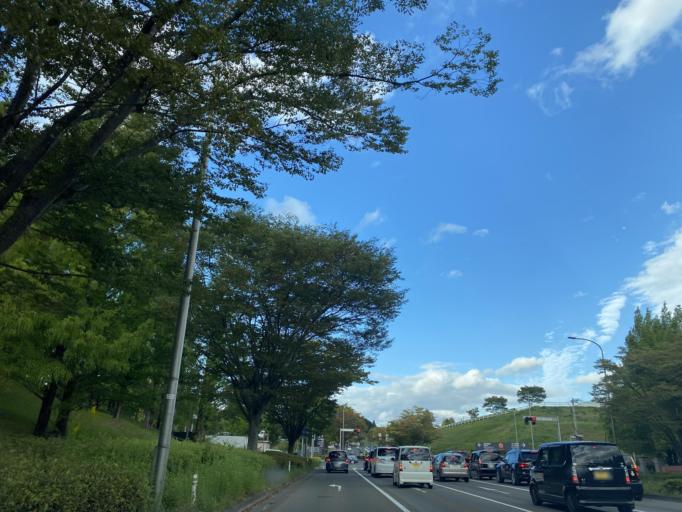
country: JP
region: Miyagi
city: Tomiya
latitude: 38.3426
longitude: 140.8390
